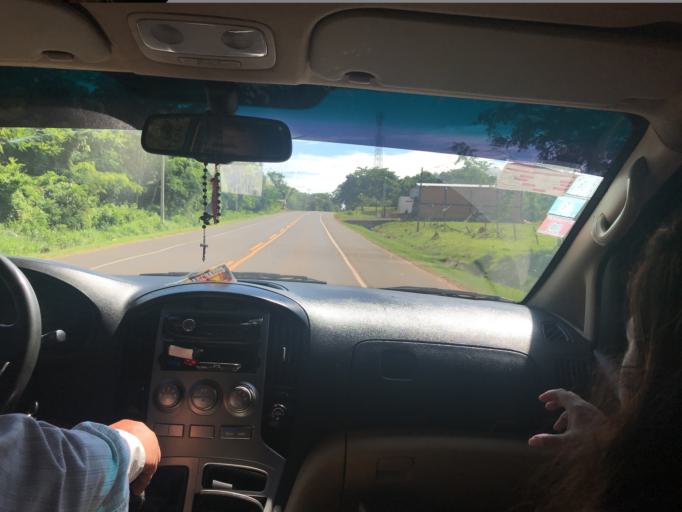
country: PY
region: San Pedro
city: Union
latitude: -24.6805
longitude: -56.4657
